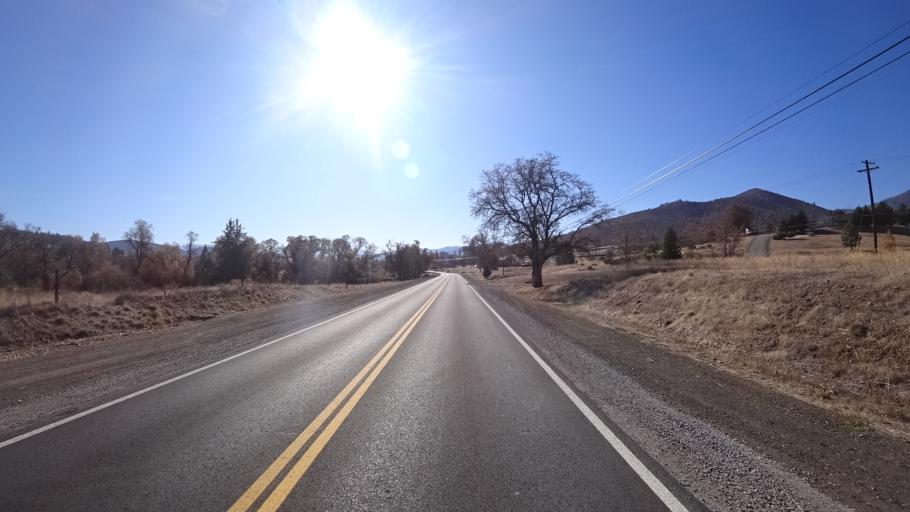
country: US
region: California
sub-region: Siskiyou County
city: Yreka
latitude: 41.7585
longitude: -122.6245
